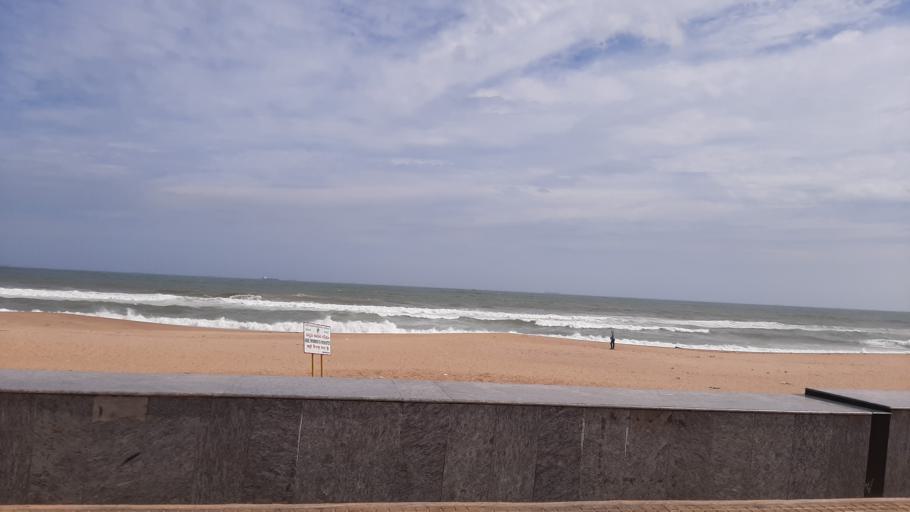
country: IN
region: Andhra Pradesh
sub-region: Vishakhapatnam
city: Yarada
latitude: 17.7186
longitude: 83.3326
